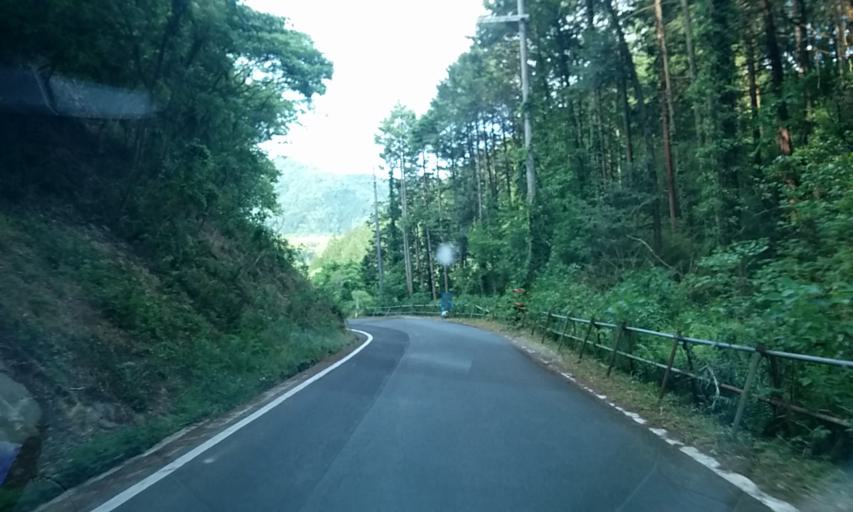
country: JP
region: Kyoto
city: Ayabe
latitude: 35.3575
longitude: 135.2065
